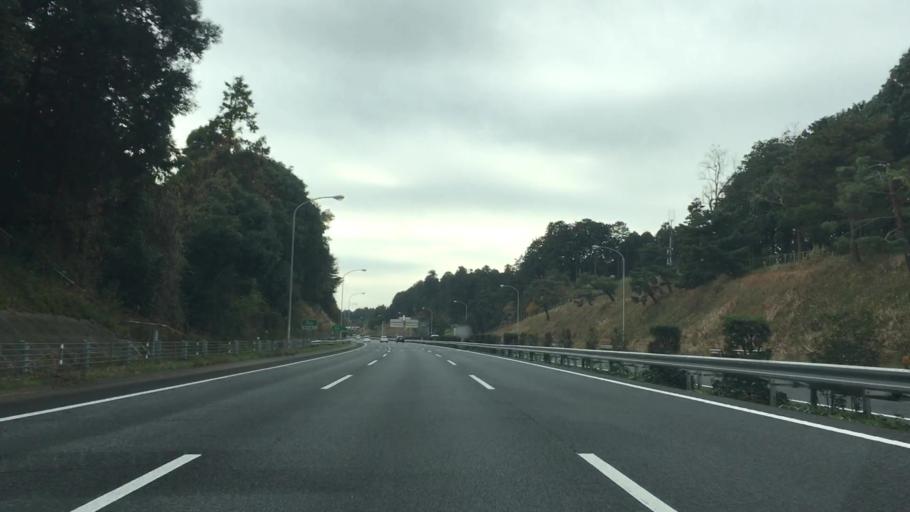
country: JP
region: Chiba
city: Narita
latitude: 35.7624
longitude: 140.3236
